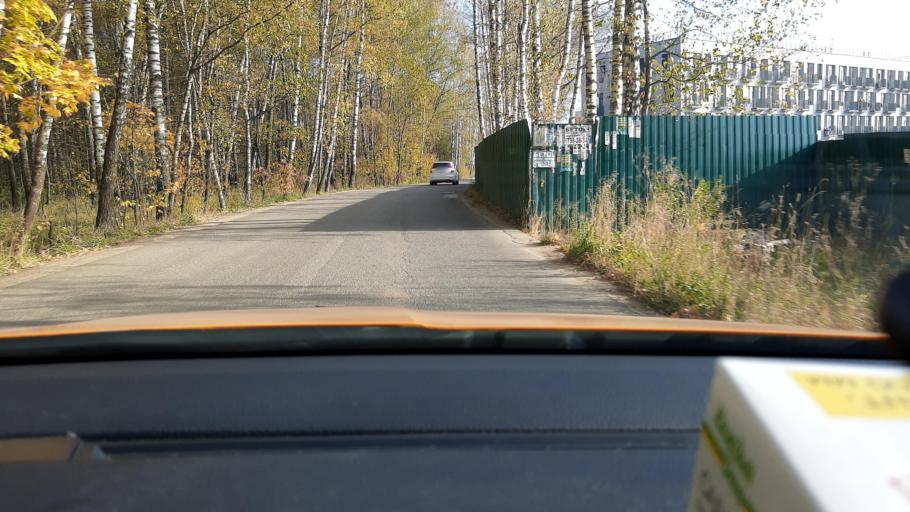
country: RU
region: Moskovskaya
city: Gorki-Leninskiye
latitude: 55.5264
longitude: 37.7929
